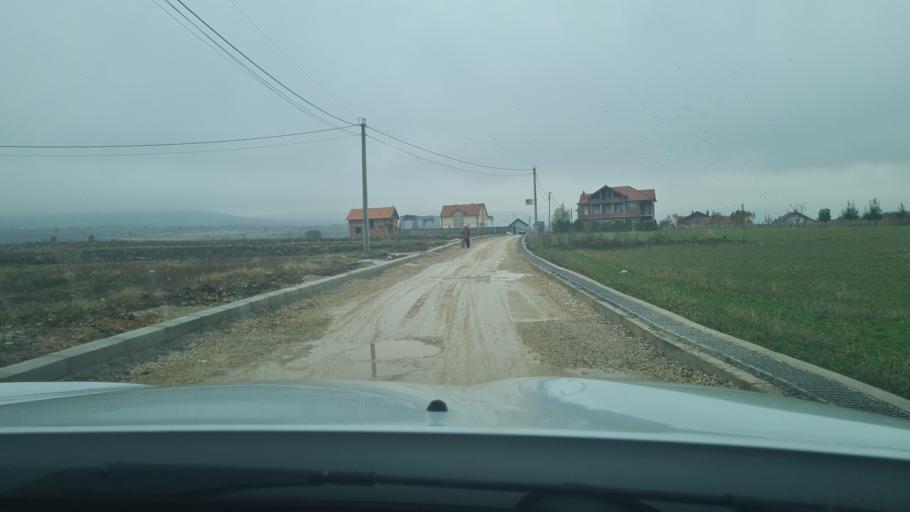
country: MK
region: Opstina Lipkovo
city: Matejche
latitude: 42.1119
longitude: 21.6134
